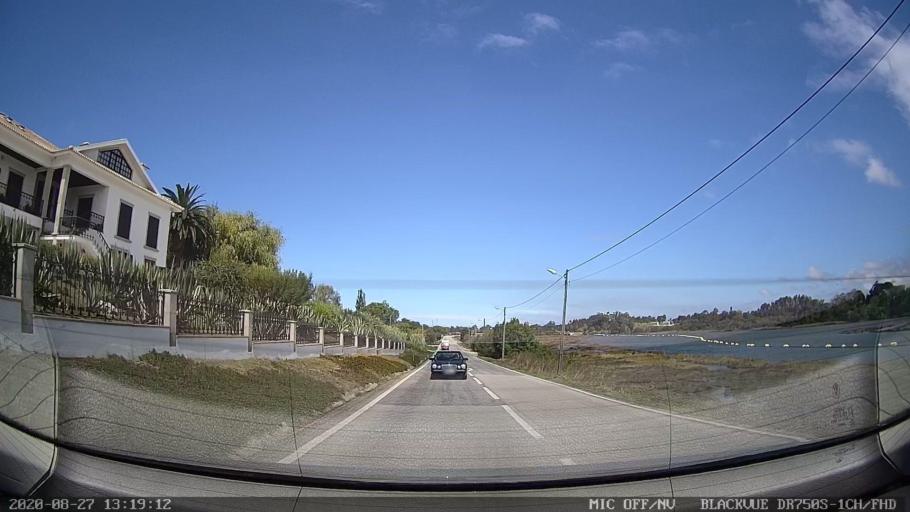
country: PT
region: Aveiro
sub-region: Vagos
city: Vagos
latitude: 40.5664
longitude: -8.6825
